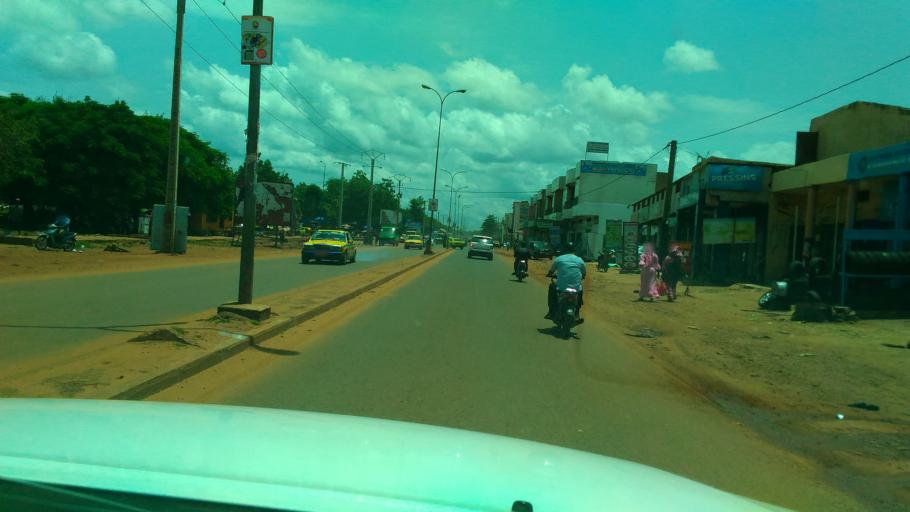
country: ML
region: Bamako
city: Bamako
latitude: 12.6667
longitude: -7.9301
